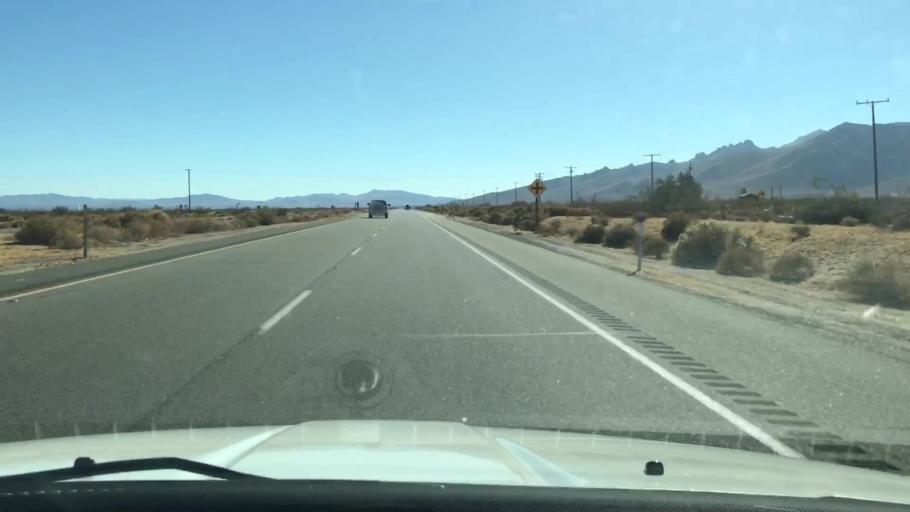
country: US
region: California
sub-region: Kern County
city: Inyokern
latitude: 35.7785
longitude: -117.8720
